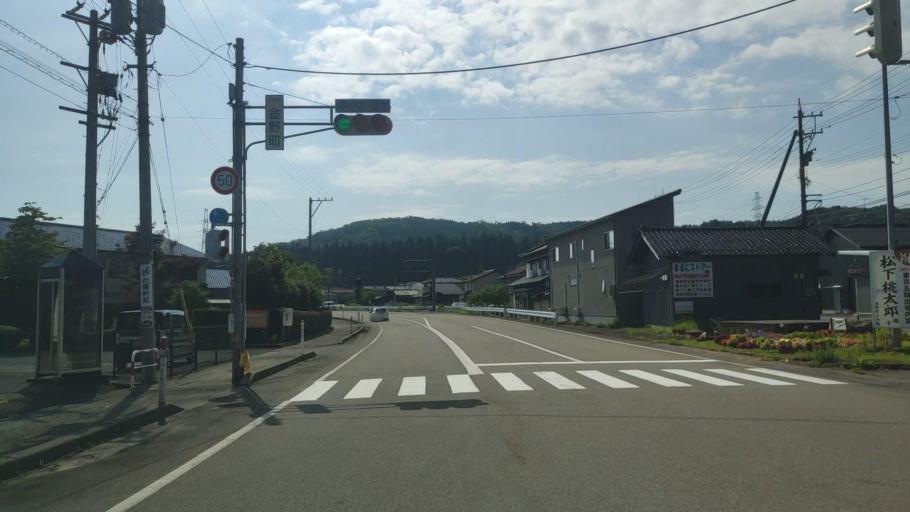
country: JP
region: Ishikawa
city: Komatsu
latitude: 36.3584
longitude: 136.4934
